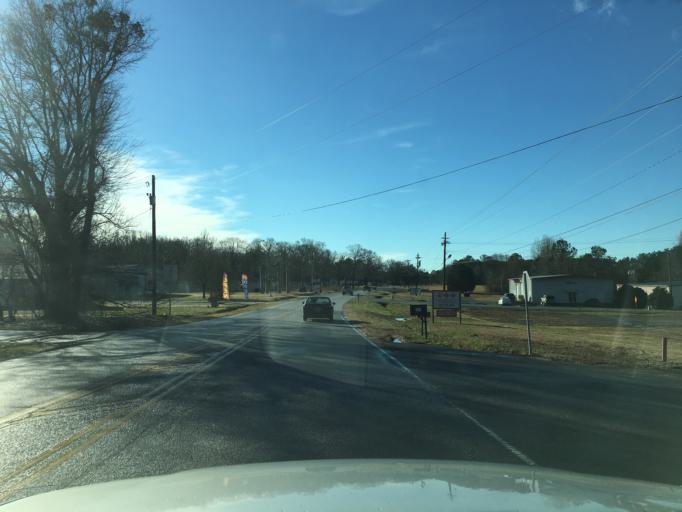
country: US
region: South Carolina
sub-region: Spartanburg County
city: Cowpens
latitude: 35.0149
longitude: -81.8726
